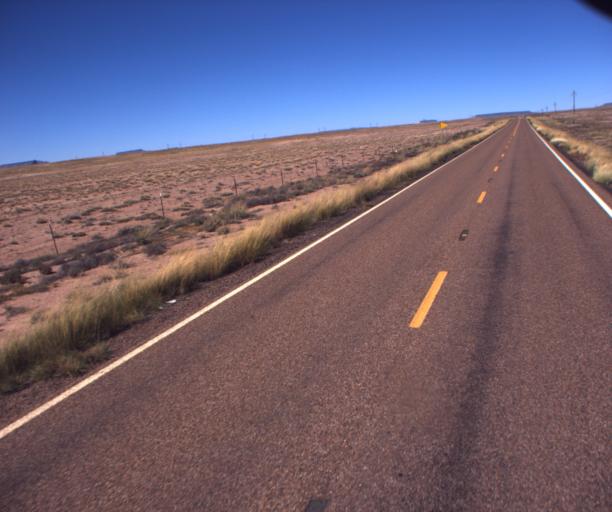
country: US
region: Arizona
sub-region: Navajo County
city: Holbrook
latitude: 35.1126
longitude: -110.0939
